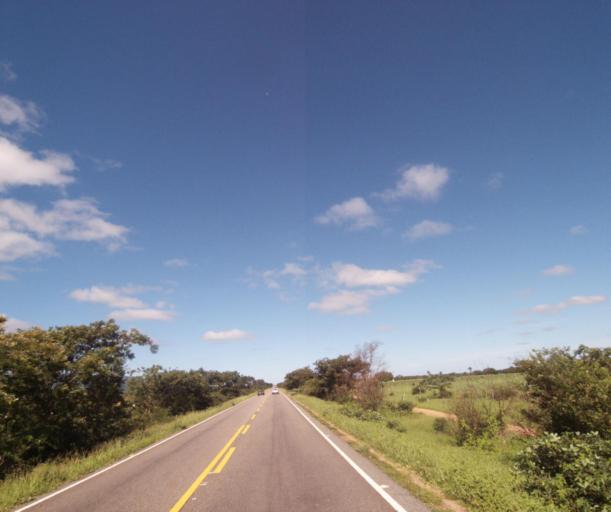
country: BR
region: Bahia
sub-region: Palmas De Monte Alto
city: Palmas de Monte Alto
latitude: -14.2406
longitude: -43.0515
